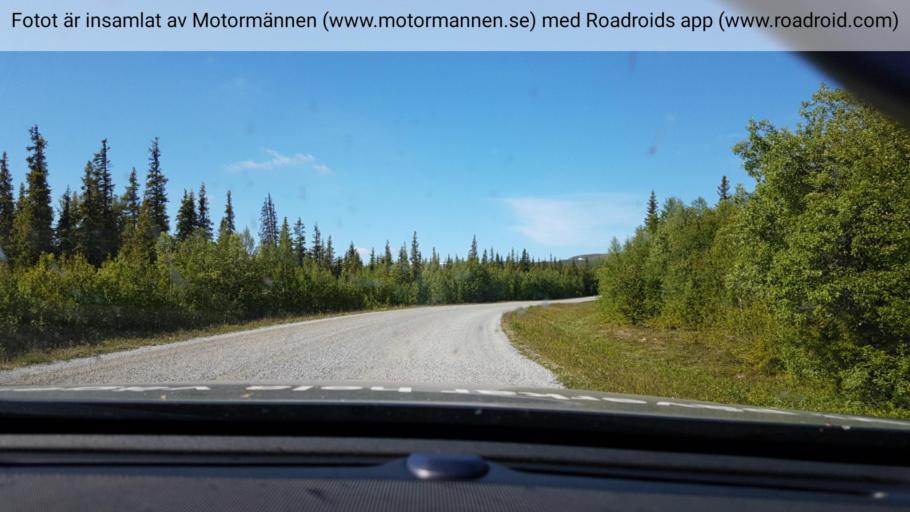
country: SE
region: Vaesterbotten
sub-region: Vilhelmina Kommun
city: Sjoberg
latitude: 65.2533
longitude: 15.6427
